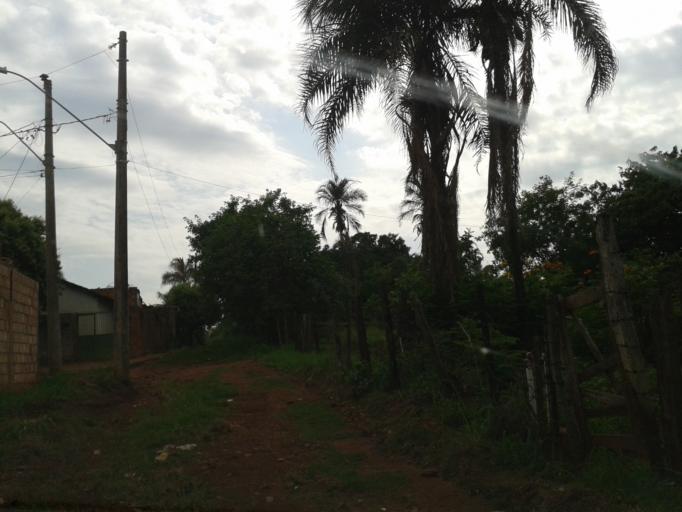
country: BR
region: Minas Gerais
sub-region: Ituiutaba
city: Ituiutaba
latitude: -18.9784
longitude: -49.4439
